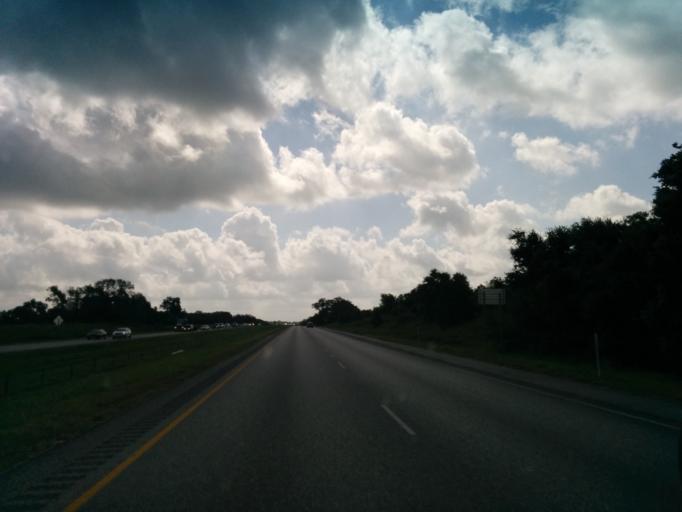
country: US
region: Texas
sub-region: Fayette County
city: Schulenburg
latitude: 29.6914
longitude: -96.9976
